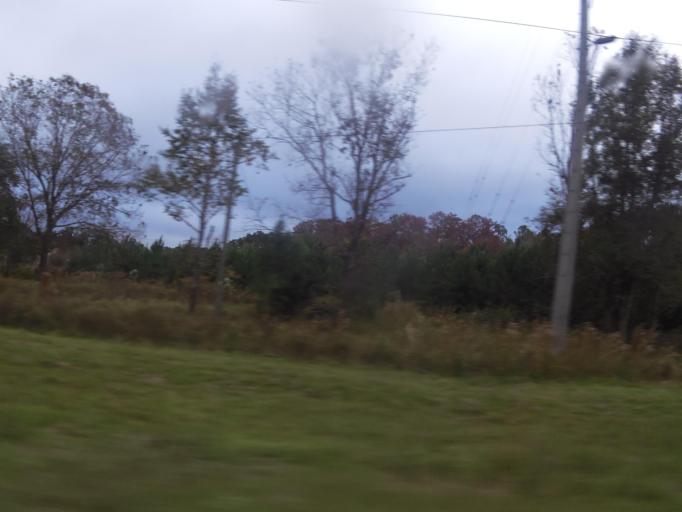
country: US
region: Georgia
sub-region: Charlton County
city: Folkston
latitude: 30.7764
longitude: -82.0551
